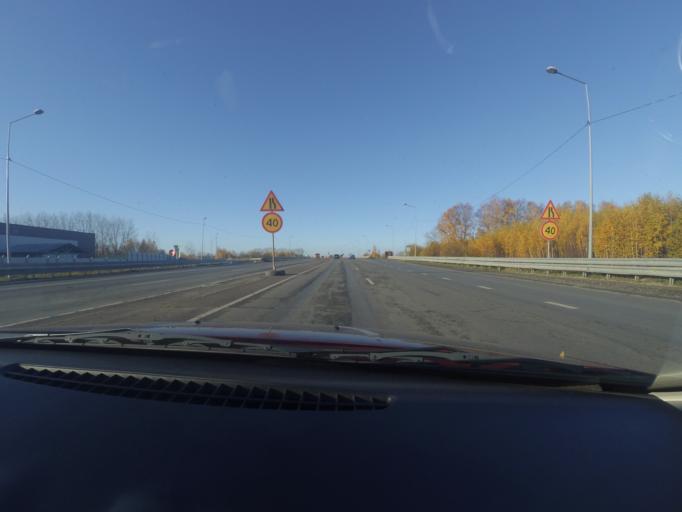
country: RU
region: Nizjnij Novgorod
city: Burevestnik
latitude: 56.1743
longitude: 43.7548
